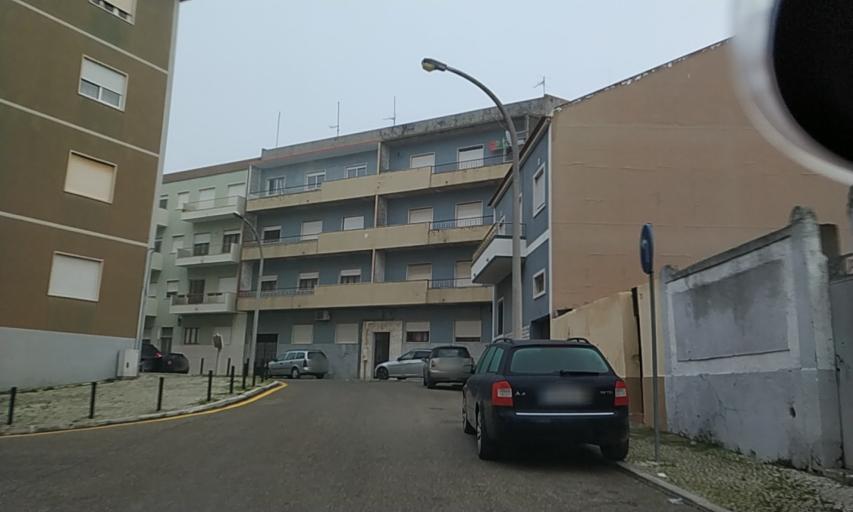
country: PT
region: Setubal
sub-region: Setubal
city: Setubal
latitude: 38.5228
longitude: -8.8805
